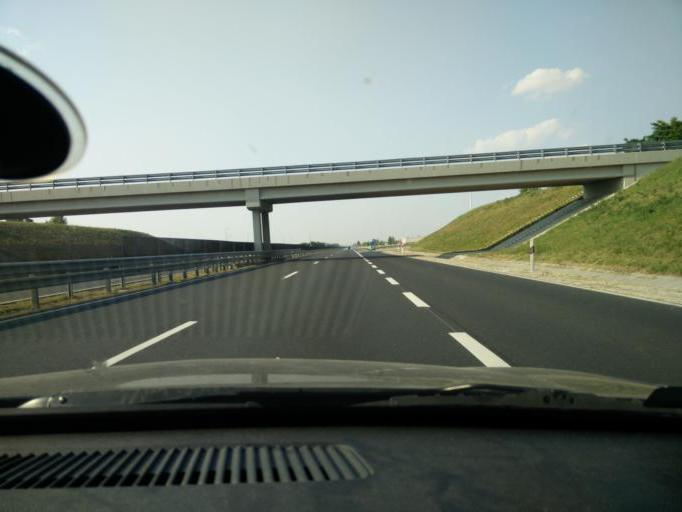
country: HU
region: Fejer
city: Rackeresztur
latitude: 47.2823
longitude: 18.8624
